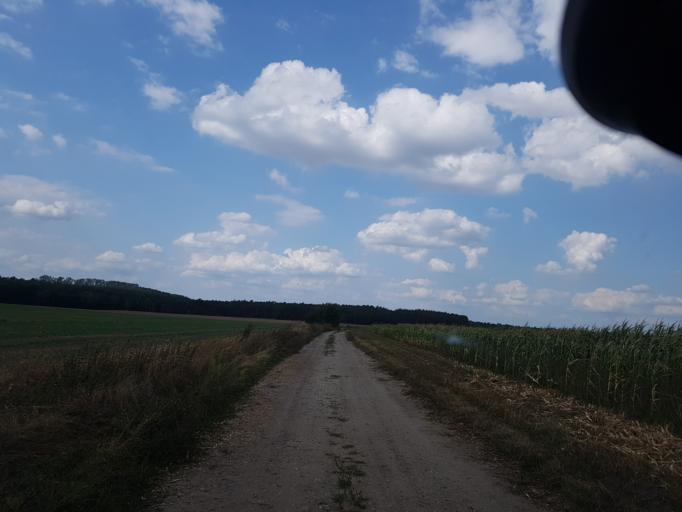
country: DE
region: Brandenburg
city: Calau
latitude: 51.7559
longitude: 13.9516
